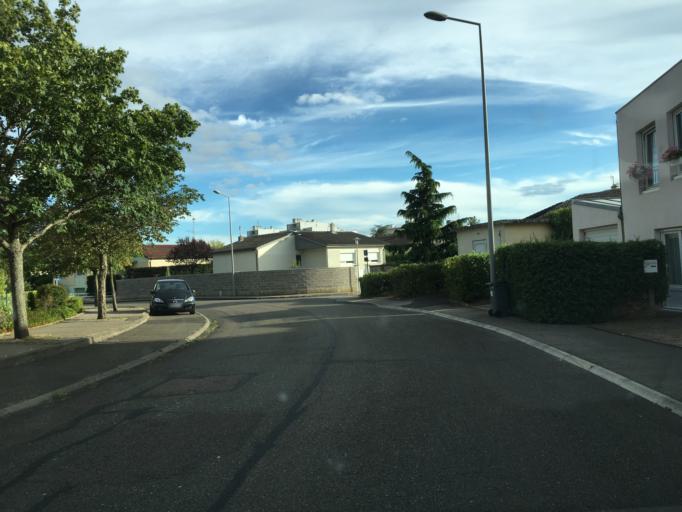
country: FR
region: Bourgogne
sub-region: Departement de la Cote-d'Or
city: Daix
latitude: 47.3418
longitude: 4.9918
